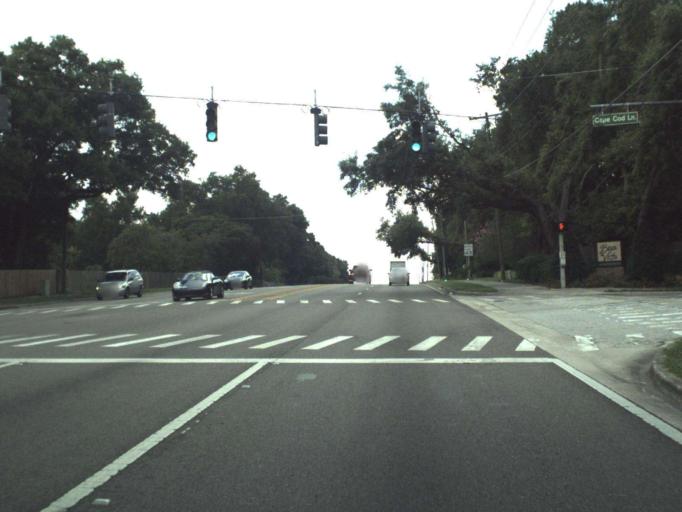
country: US
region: Florida
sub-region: Seminole County
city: Forest City
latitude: 28.6723
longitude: -81.4192
